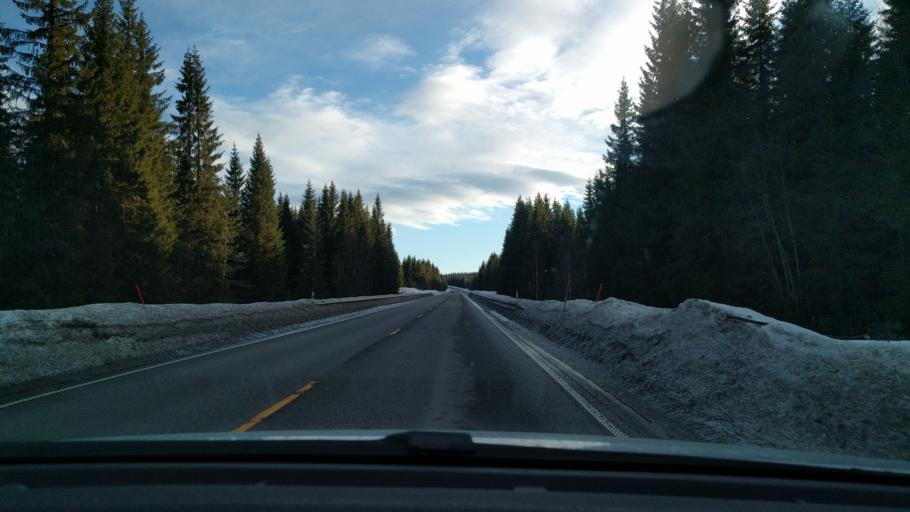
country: NO
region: Hedmark
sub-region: Trysil
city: Innbygda
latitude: 61.0800
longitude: 11.9789
